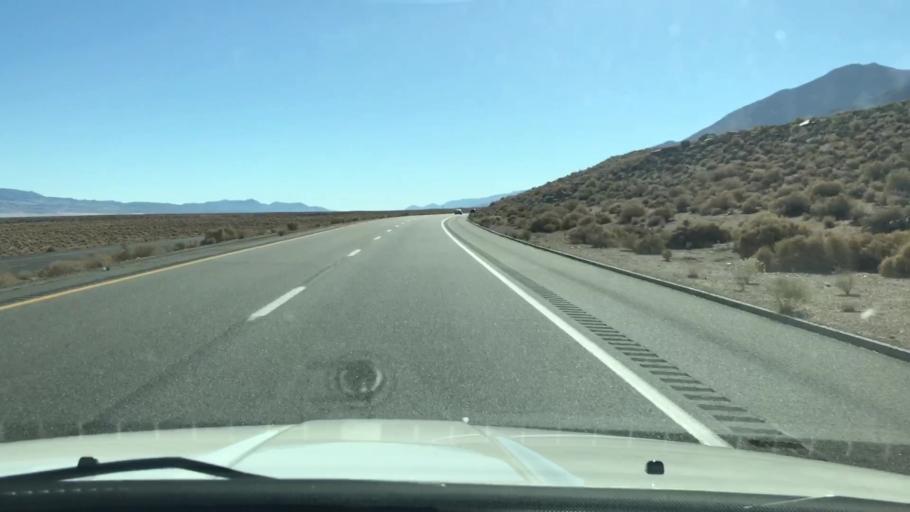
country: US
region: California
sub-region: Inyo County
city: Lone Pine
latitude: 36.4535
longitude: -118.0350
